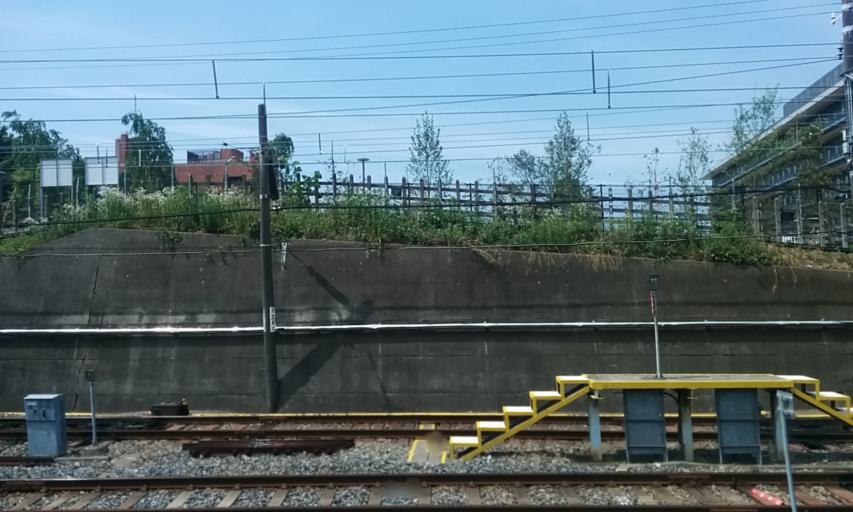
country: JP
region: Chiba
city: Funabashi
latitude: 35.6820
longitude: 140.0285
